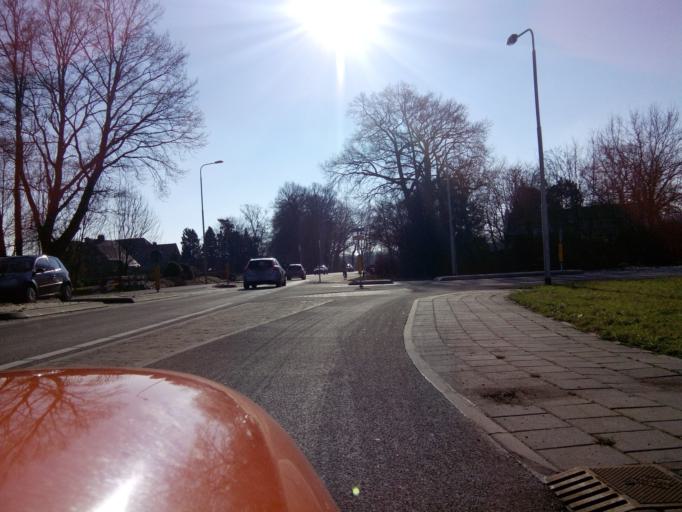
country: NL
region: Gelderland
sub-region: Gemeente Barneveld
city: Barneveld
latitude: 52.1598
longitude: 5.6009
